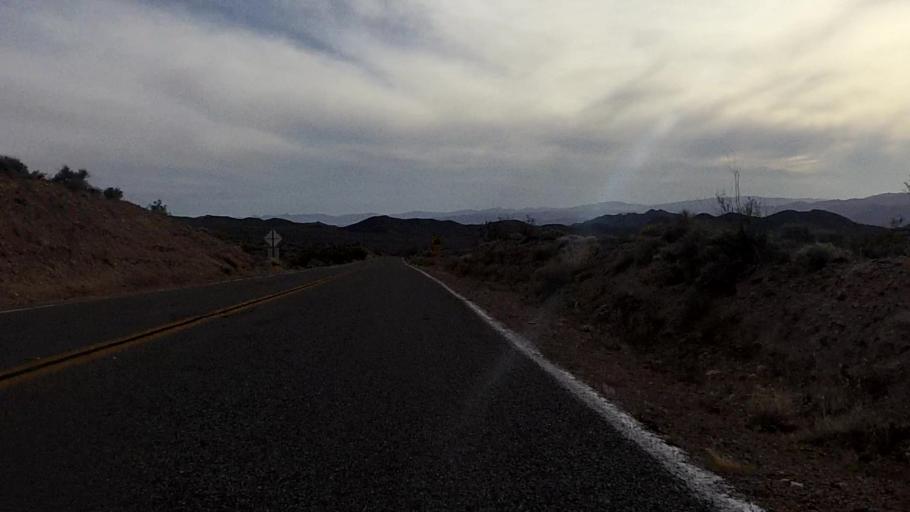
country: US
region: Nevada
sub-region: Nye County
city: Pahrump
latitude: 35.9210
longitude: -116.4349
